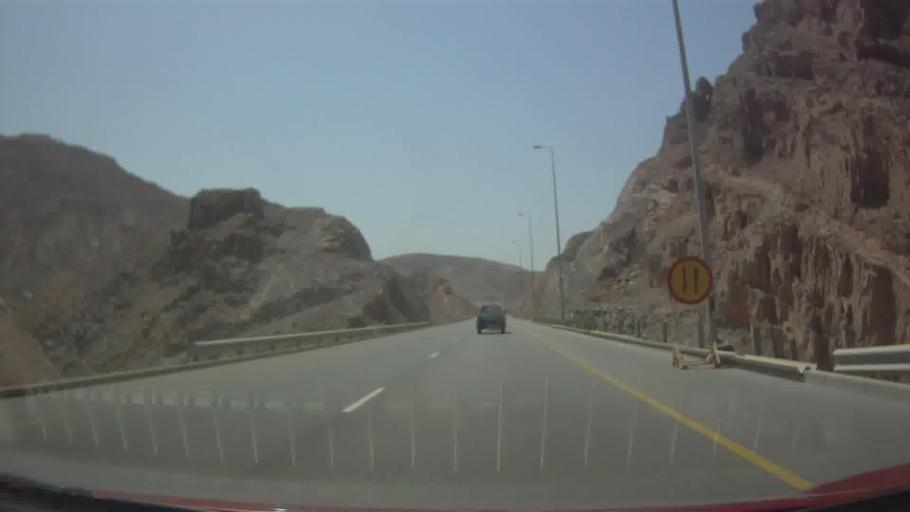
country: OM
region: Muhafazat Masqat
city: Muscat
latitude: 23.5272
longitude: 58.6437
